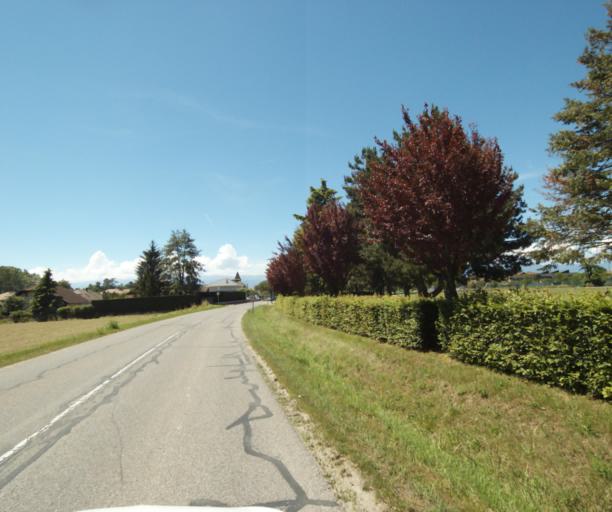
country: FR
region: Rhone-Alpes
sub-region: Departement de la Haute-Savoie
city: Veigy-Foncenex
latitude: 46.2683
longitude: 6.2603
